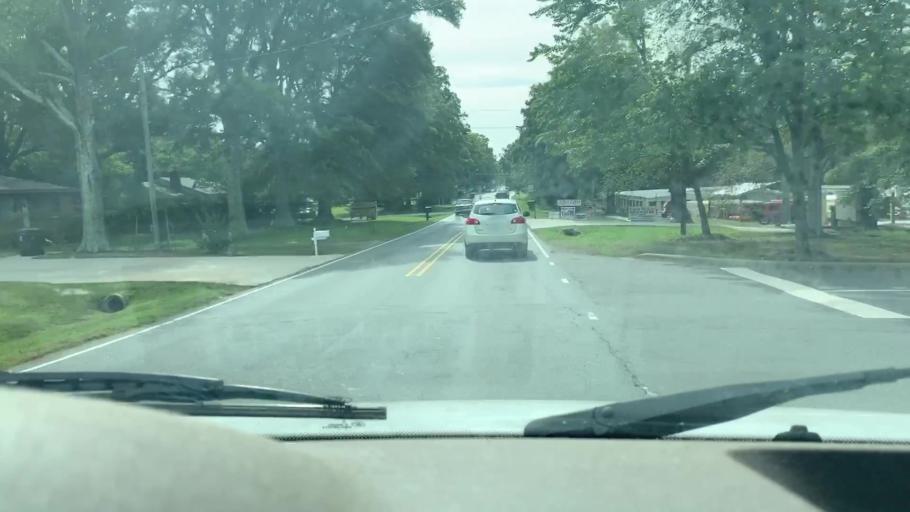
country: US
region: North Carolina
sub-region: Mecklenburg County
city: Huntersville
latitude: 35.4333
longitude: -80.8436
